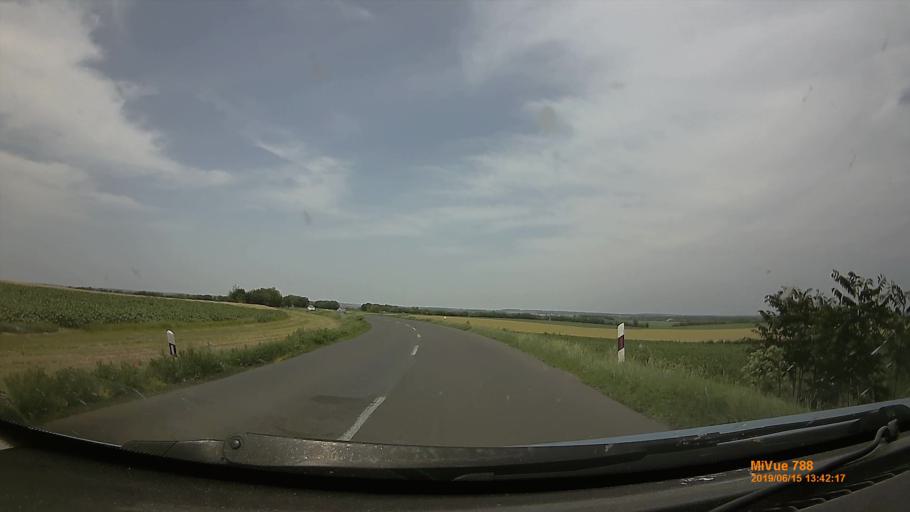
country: HU
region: Tolna
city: Iregszemcse
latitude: 46.6626
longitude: 18.1878
